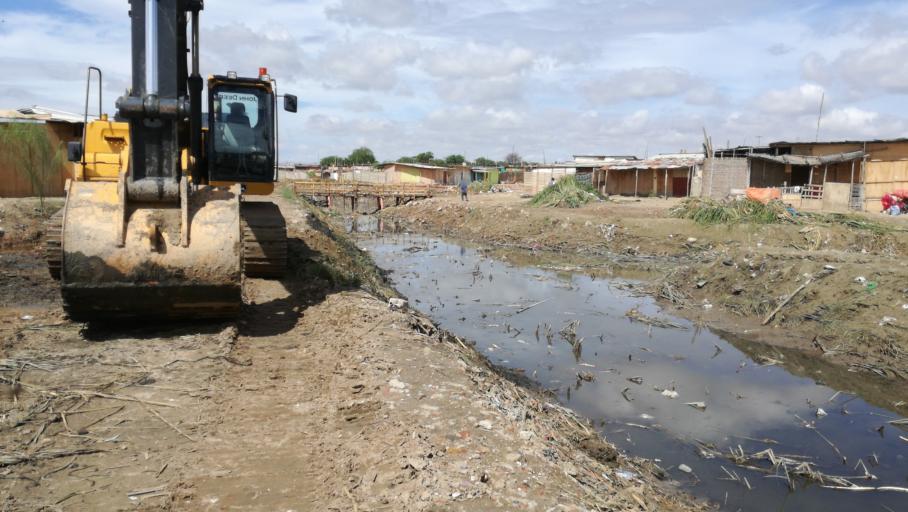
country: PE
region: Piura
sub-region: Provincia de Piura
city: Piura
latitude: -5.2016
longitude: -80.6518
